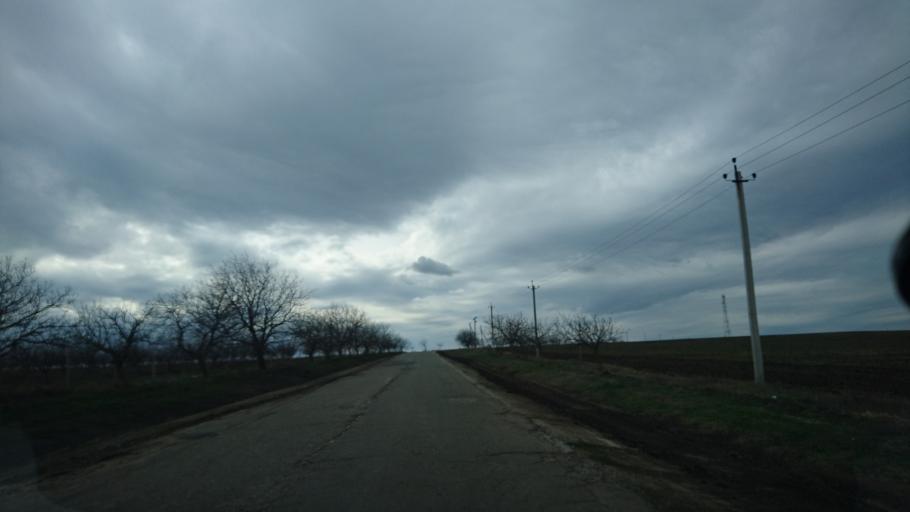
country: MD
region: Cantemir
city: Visniovca
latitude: 46.3254
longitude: 28.4772
